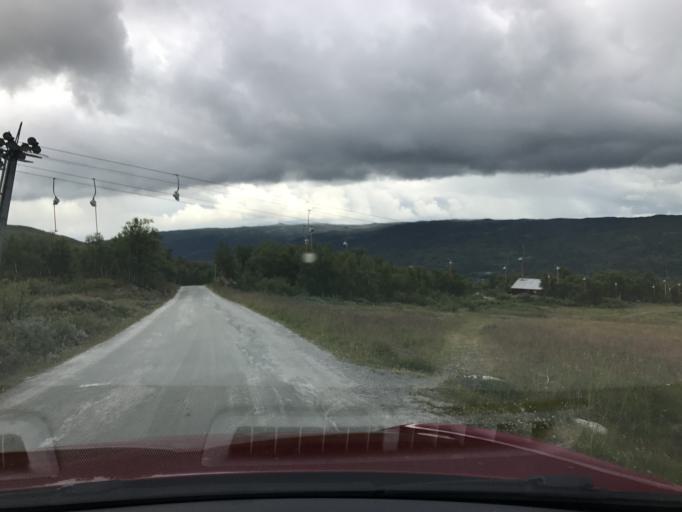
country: NO
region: Buskerud
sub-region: Hol
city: Geilo
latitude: 60.5490
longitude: 8.1922
